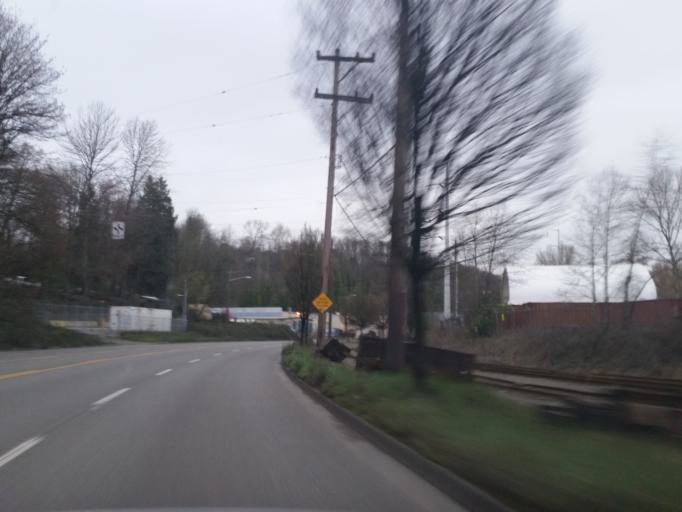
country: US
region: Washington
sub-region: King County
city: White Center
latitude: 47.5566
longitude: -122.3508
